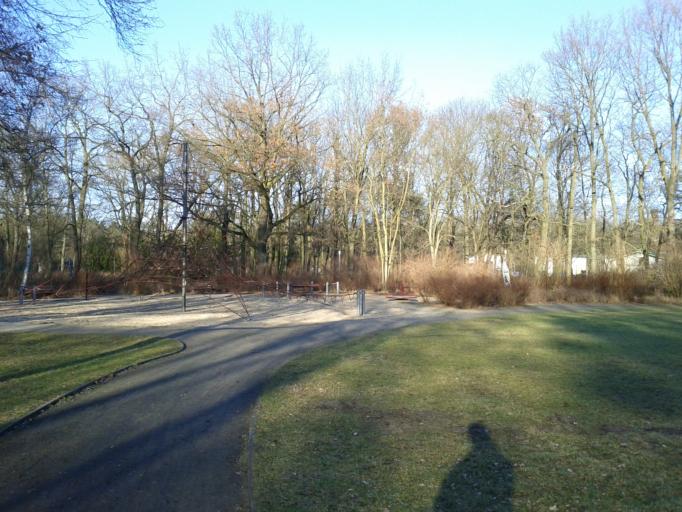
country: DE
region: Berlin
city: Friedrichshagen
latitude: 52.4585
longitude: 13.6246
